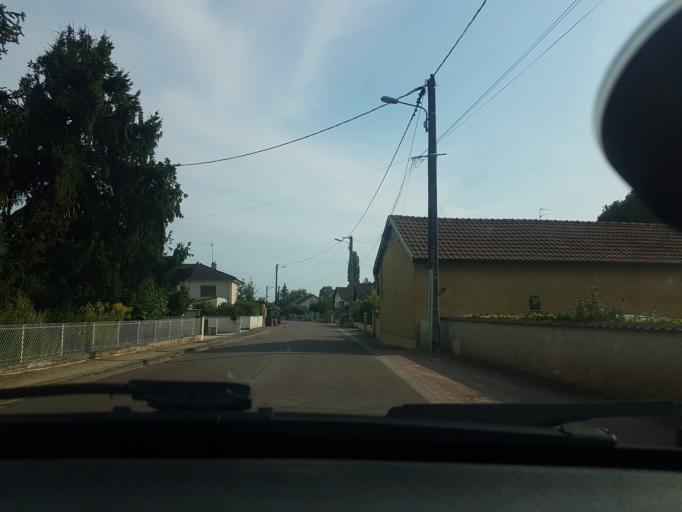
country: FR
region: Bourgogne
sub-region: Departement de Saone-et-Loire
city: Saint-Marcel
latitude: 46.7674
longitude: 4.8894
